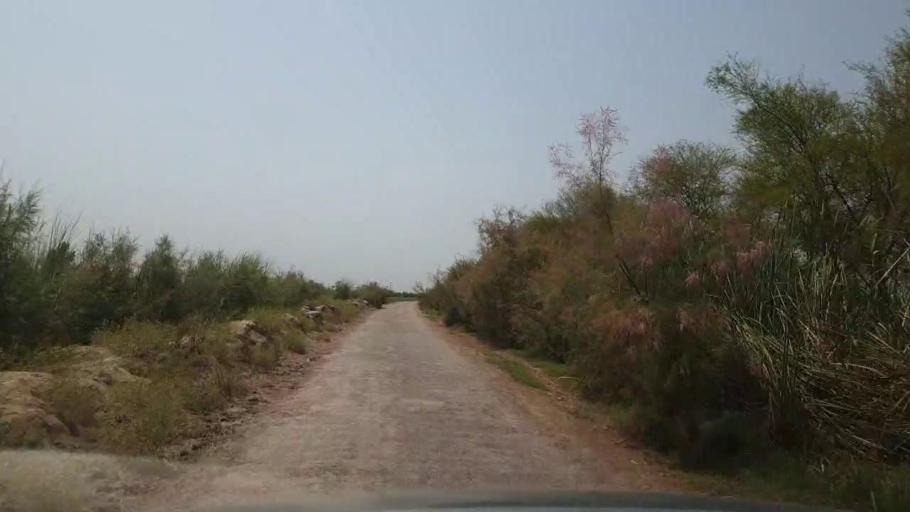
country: PK
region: Sindh
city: Garhi Yasin
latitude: 27.8944
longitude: 68.4504
